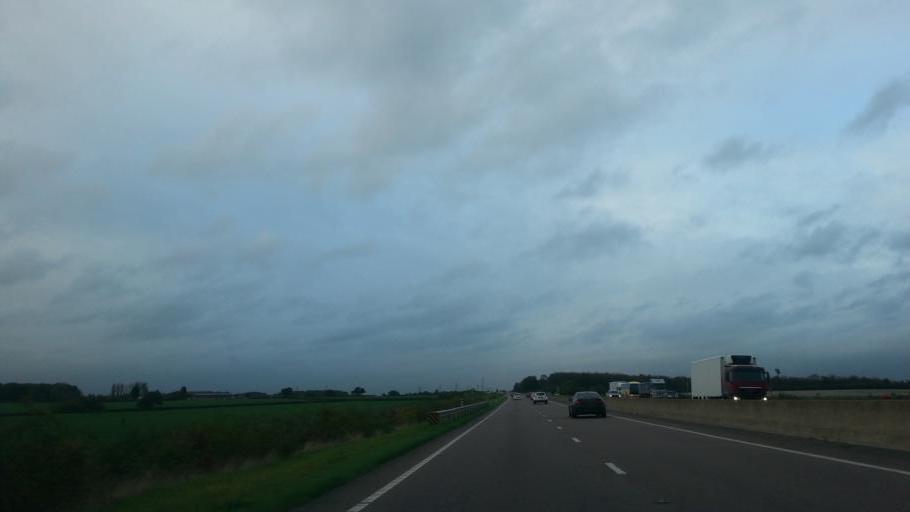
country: GB
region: England
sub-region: Nottinghamshire
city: Cotgrave
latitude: 52.8785
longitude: -1.0273
